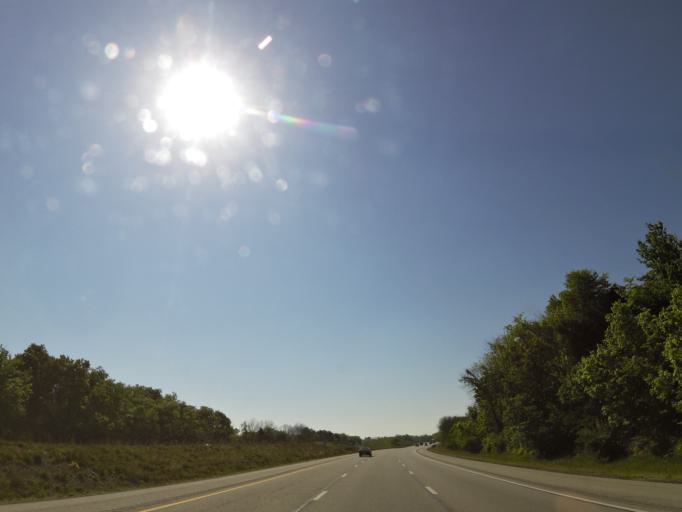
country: US
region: Kentucky
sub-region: Shelby County
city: Shelbyville
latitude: 38.1685
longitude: -85.1433
